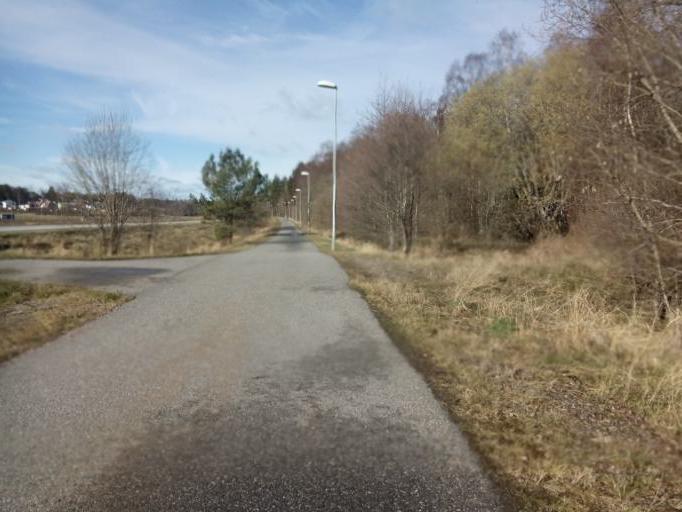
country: SE
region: Soedermanland
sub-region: Nykopings Kommun
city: Nykoping
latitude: 58.7662
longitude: 17.0635
